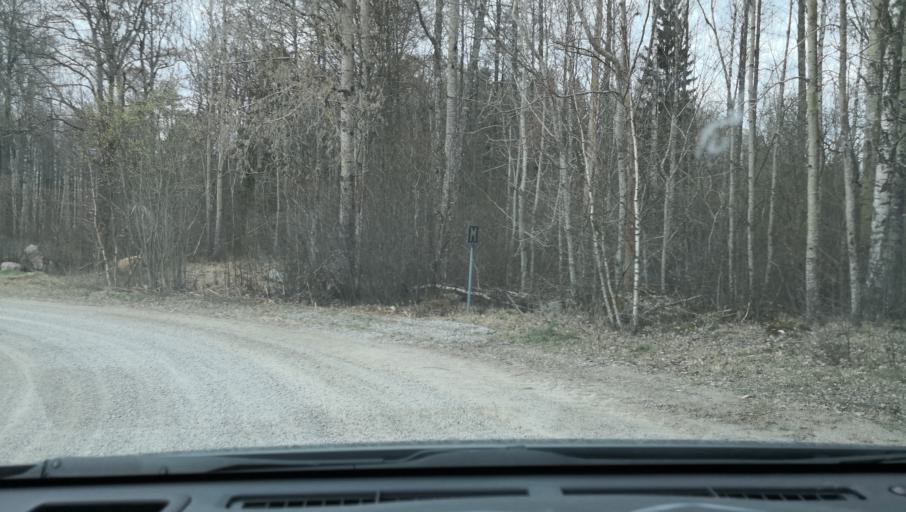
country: SE
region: Soedermanland
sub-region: Katrineholms Kommun
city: Katrineholm
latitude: 59.1309
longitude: 16.1677
